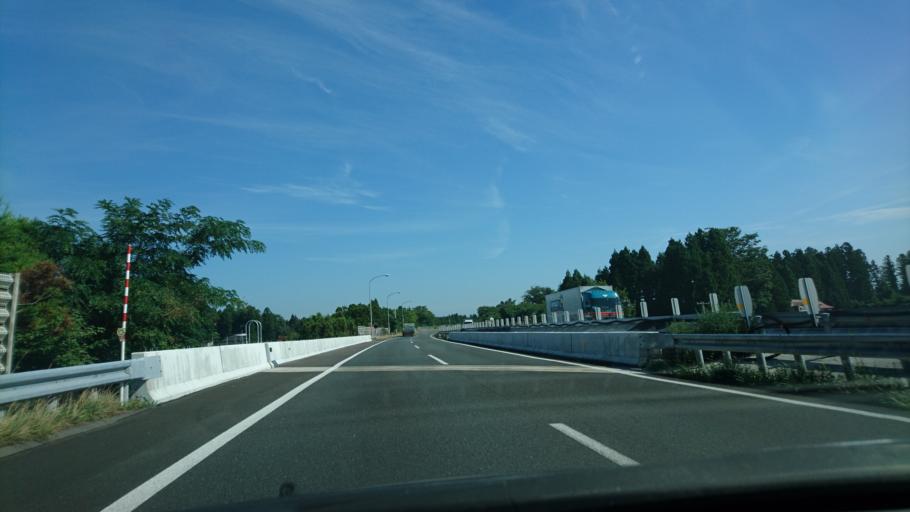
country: JP
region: Iwate
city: Mizusawa
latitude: 39.0739
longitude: 141.0998
